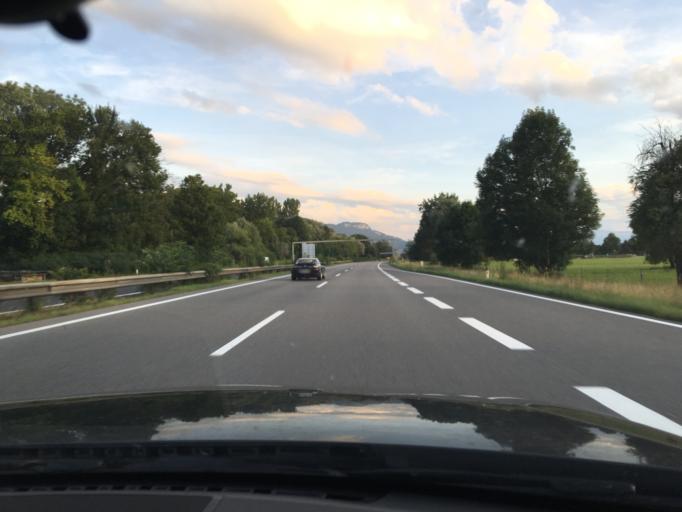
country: AT
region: Vorarlberg
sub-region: Politischer Bezirk Dornbirn
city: Dornbirn
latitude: 47.4331
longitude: 9.7207
